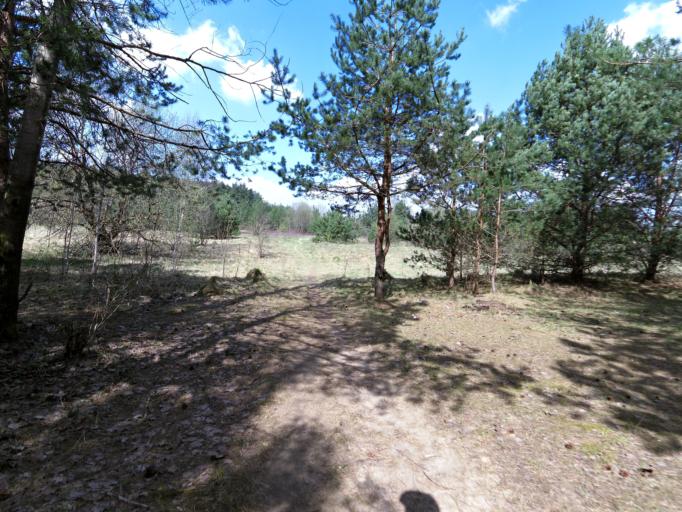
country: LT
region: Vilnius County
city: Pilaite
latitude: 54.6982
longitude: 25.2046
